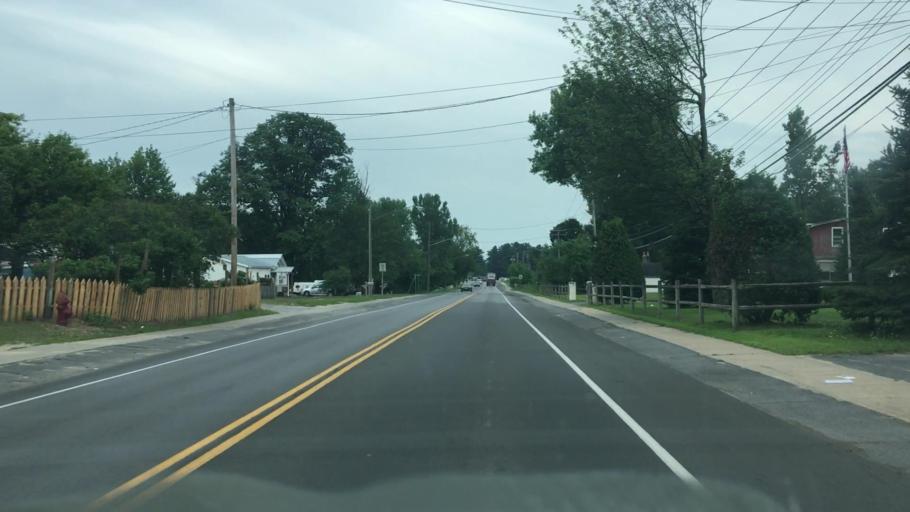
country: US
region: New York
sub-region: Clinton County
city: Plattsburgh West
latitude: 44.6798
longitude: -73.5060
